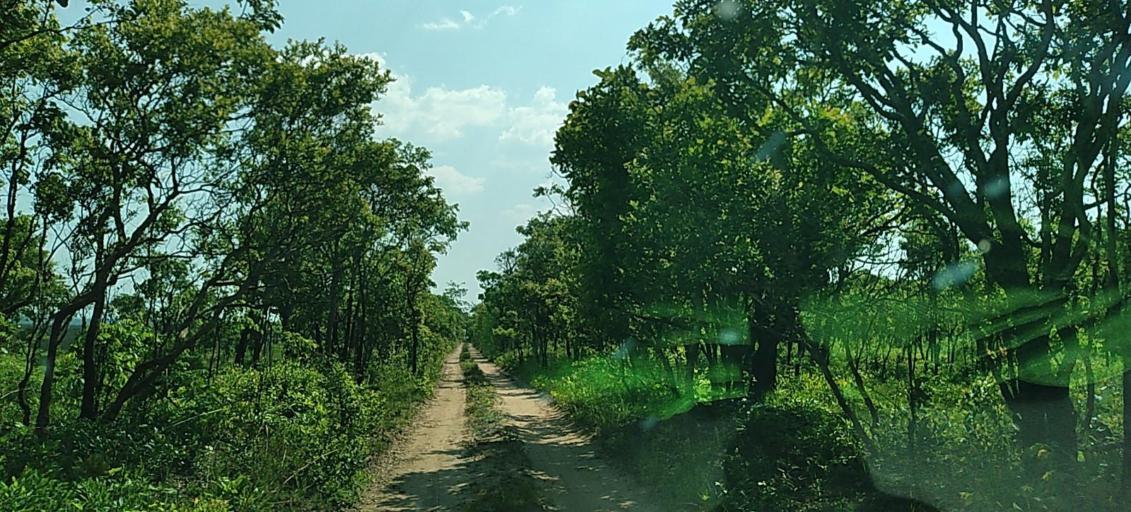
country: ZM
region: North-Western
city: Mwinilunga
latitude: -11.2716
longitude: 24.9895
